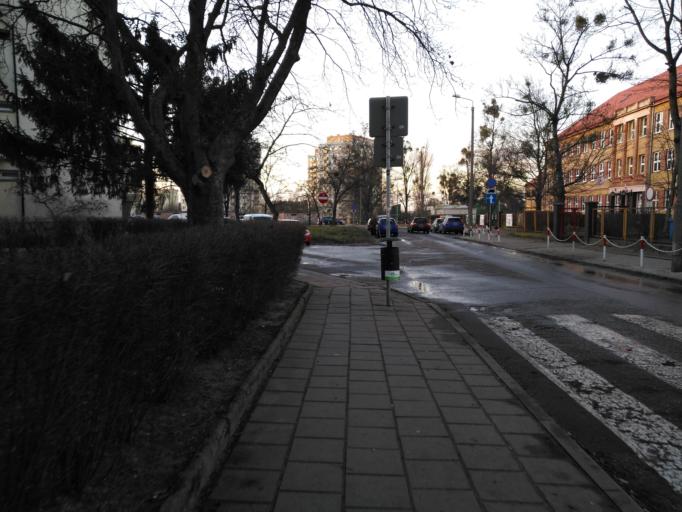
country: PL
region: Kujawsko-Pomorskie
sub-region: Bydgoszcz
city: Bydgoszcz
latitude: 53.1093
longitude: 18.0570
